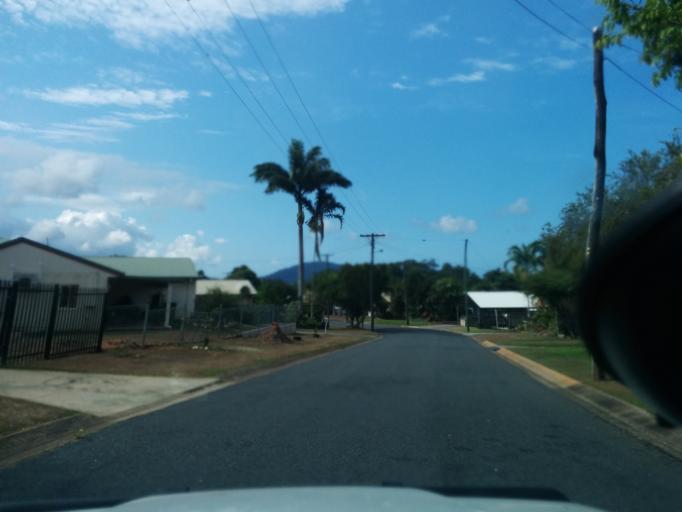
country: AU
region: Queensland
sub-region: Cairns
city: Woree
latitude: -16.9524
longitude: 145.7369
